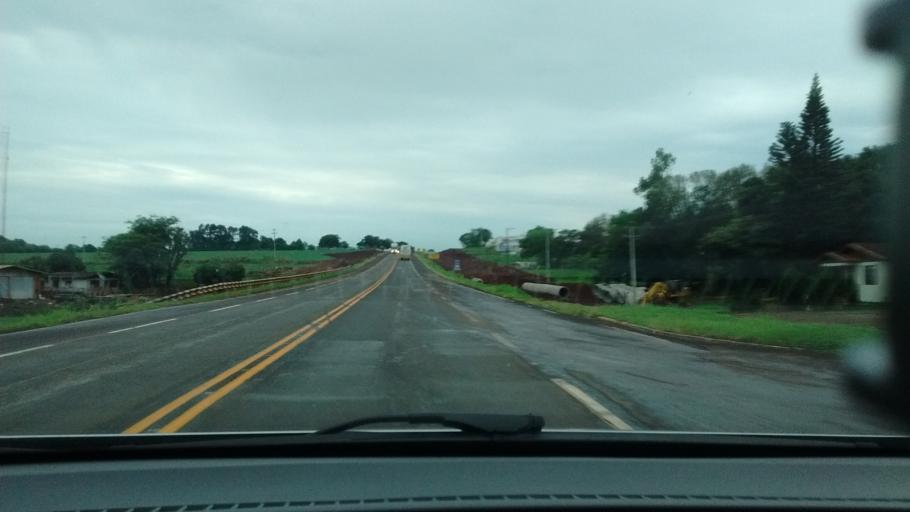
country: BR
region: Parana
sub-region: Corbelia
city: Corbelia
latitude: -24.7861
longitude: -53.2902
